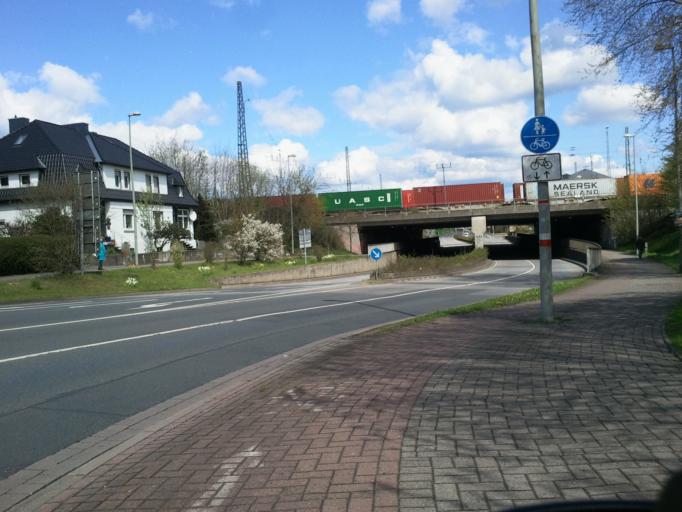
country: DE
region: Lower Saxony
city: Nienburg
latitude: 52.6418
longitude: 9.2193
